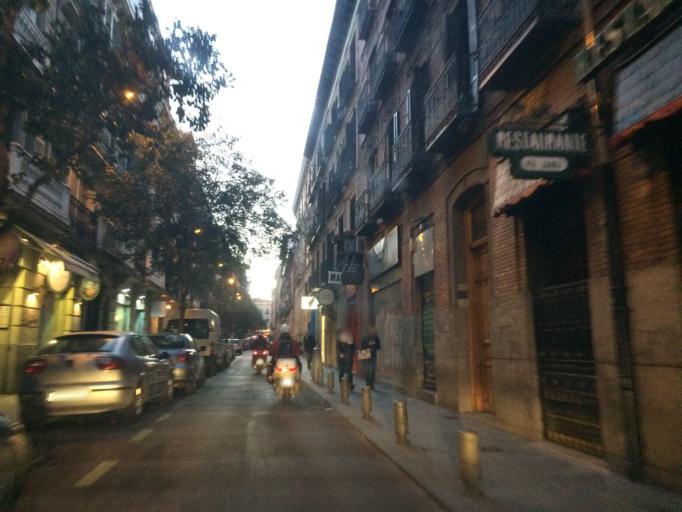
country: ES
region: Madrid
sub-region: Provincia de Madrid
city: City Center
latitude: 40.4262
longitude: -3.6979
